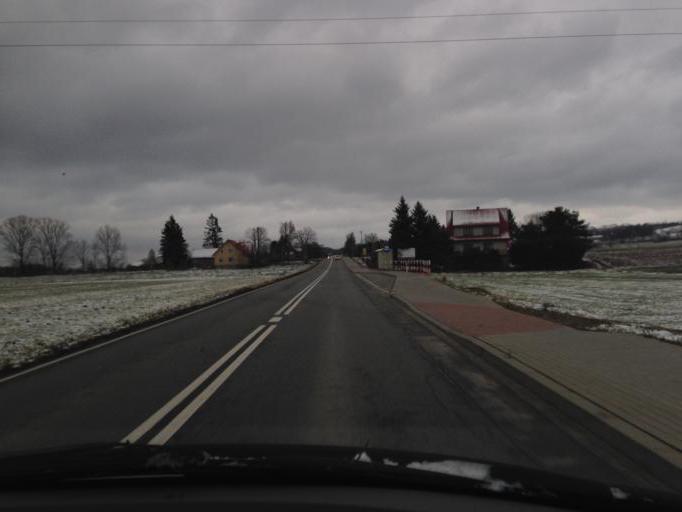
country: PL
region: Lesser Poland Voivodeship
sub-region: Powiat tarnowski
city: Zakliczyn
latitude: 49.8531
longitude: 20.8266
